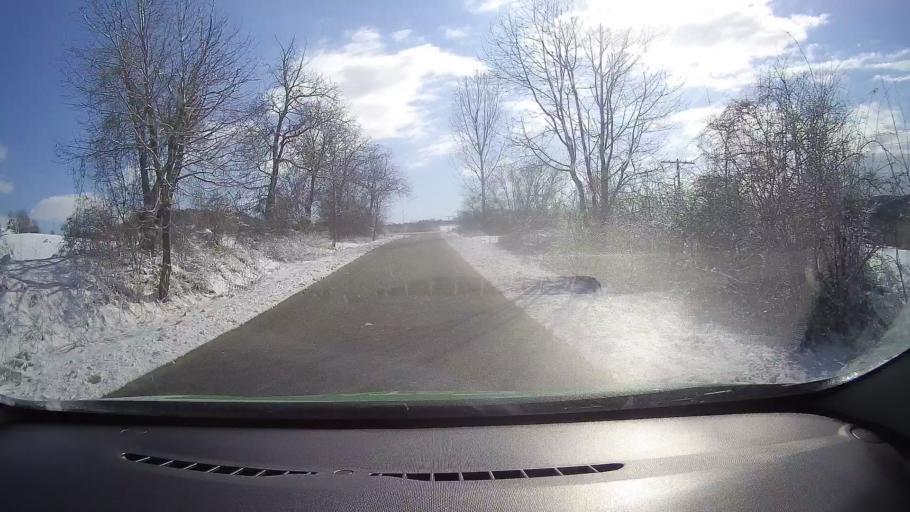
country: RO
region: Sibiu
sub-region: Comuna Mosna
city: Mosna
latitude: 46.0109
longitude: 24.4222
